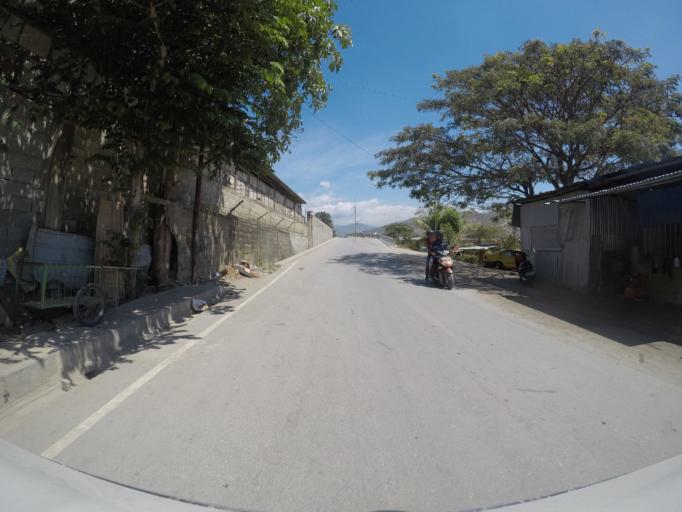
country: TL
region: Dili
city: Dili
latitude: -8.5604
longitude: 125.5353
